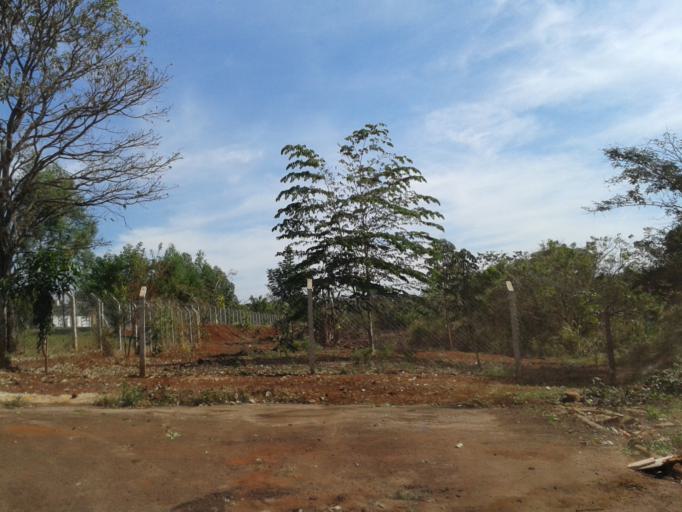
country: BR
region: Minas Gerais
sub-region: Ituiutaba
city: Ituiutaba
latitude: -18.9606
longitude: -49.4640
